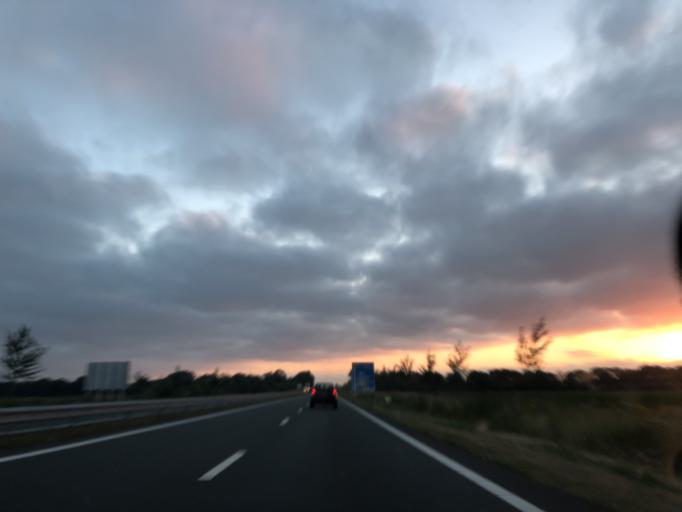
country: NL
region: Groningen
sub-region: Gemeente Veendam
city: Veendam
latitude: 53.0876
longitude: 6.8883
